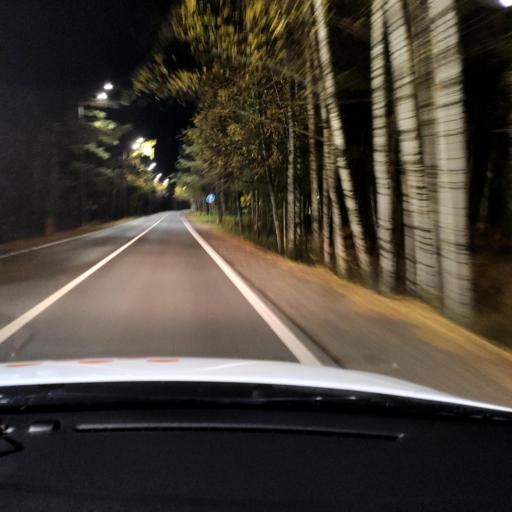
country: RU
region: Tatarstan
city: Verkhniy Uslon
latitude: 55.6326
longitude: 49.0180
